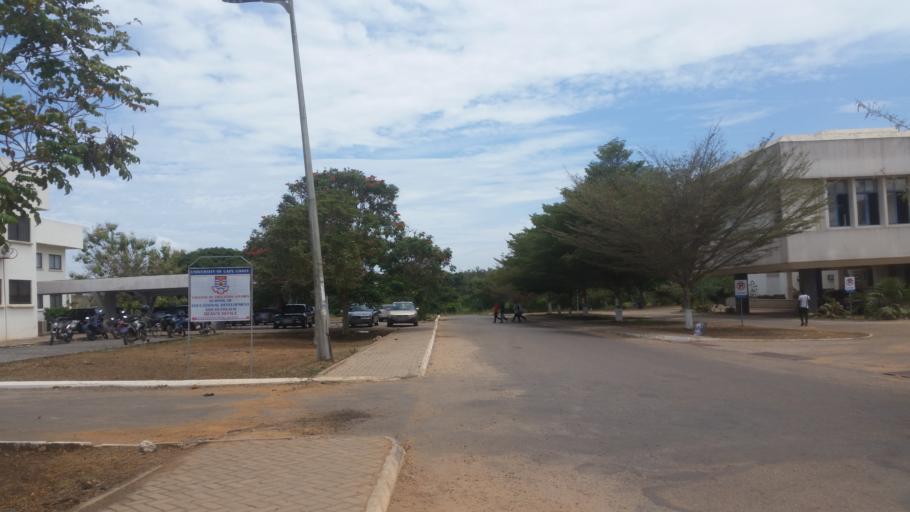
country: GH
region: Central
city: Cape Coast
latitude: 5.1191
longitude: -1.2930
